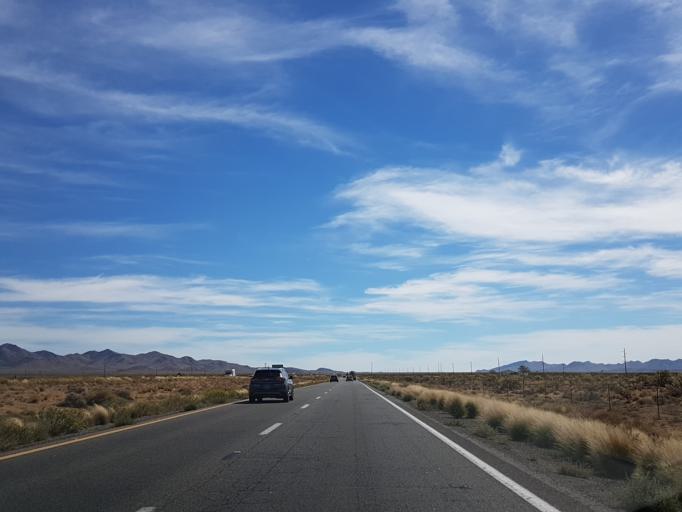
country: US
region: Arizona
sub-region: Mohave County
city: Dolan Springs
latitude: 35.5213
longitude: -114.3469
